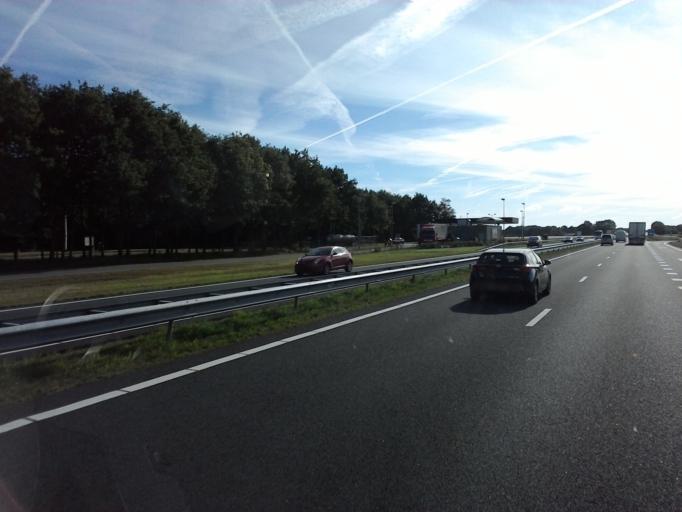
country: NL
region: Drenthe
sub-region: Gemeente Assen
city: Assen
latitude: 52.9703
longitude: 6.6129
